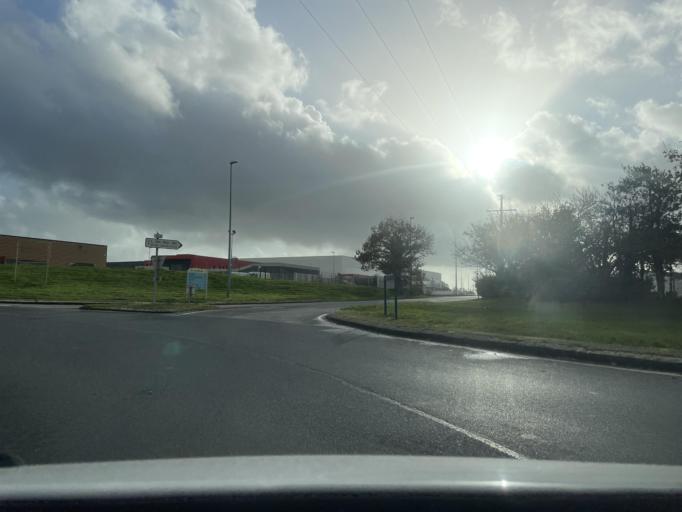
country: FR
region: Brittany
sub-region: Departement du Finistere
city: Briec
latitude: 48.1000
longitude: -4.0171
